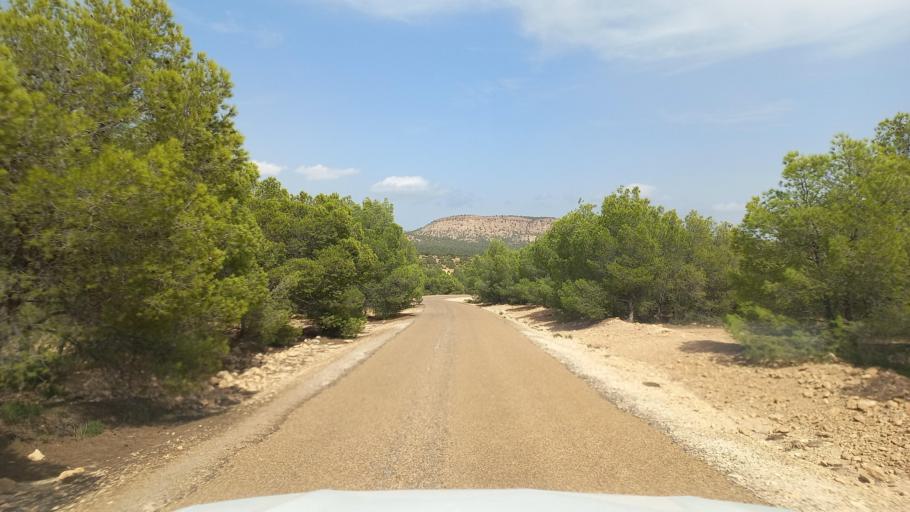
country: TN
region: Al Qasrayn
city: Sbiba
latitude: 35.4072
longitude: 8.9258
